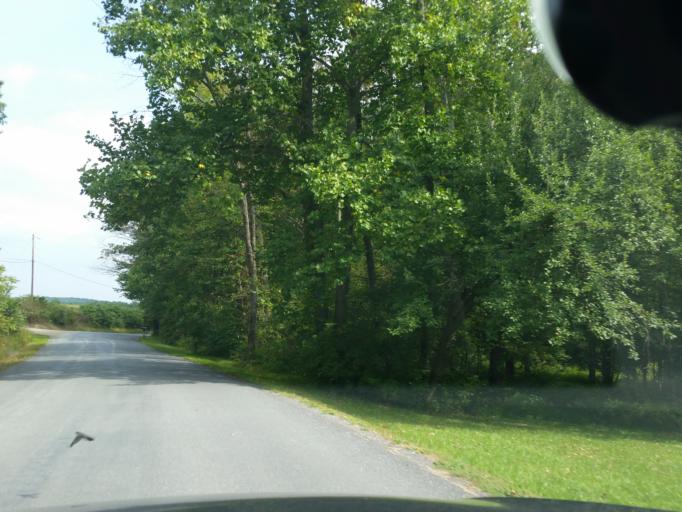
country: US
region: Pennsylvania
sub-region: Union County
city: Mifflinburg
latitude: 40.9870
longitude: -77.0515
